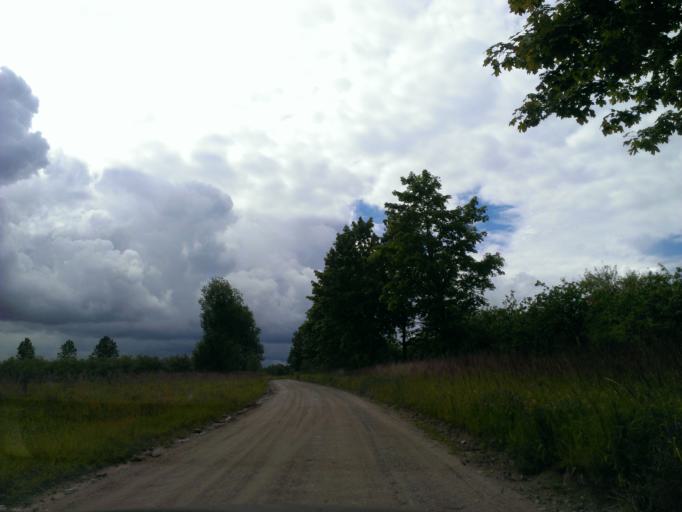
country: LV
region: Ligatne
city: Ligatne
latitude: 57.2149
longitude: 25.0232
